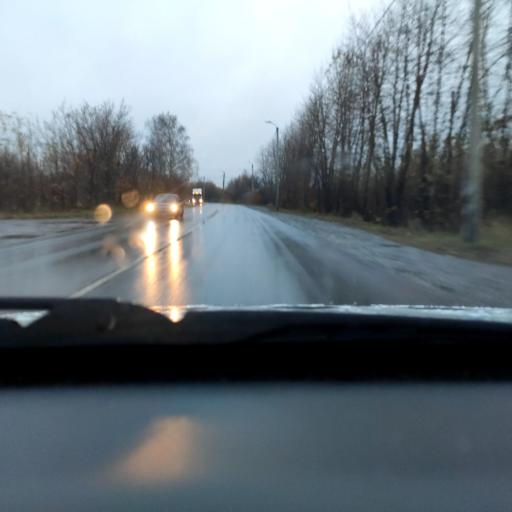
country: RU
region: Perm
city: Kondratovo
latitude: 57.9433
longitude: 56.1536
